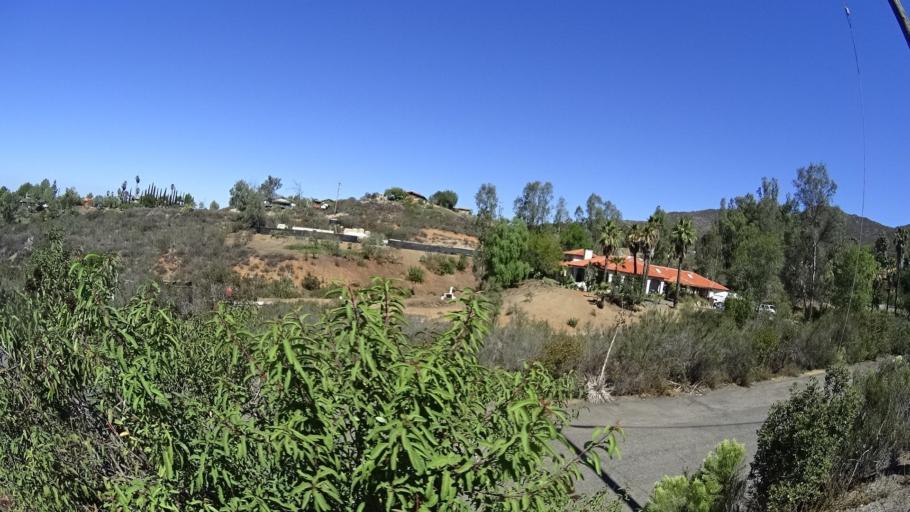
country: US
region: California
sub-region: San Diego County
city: Jamul
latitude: 32.7395
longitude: -116.8717
